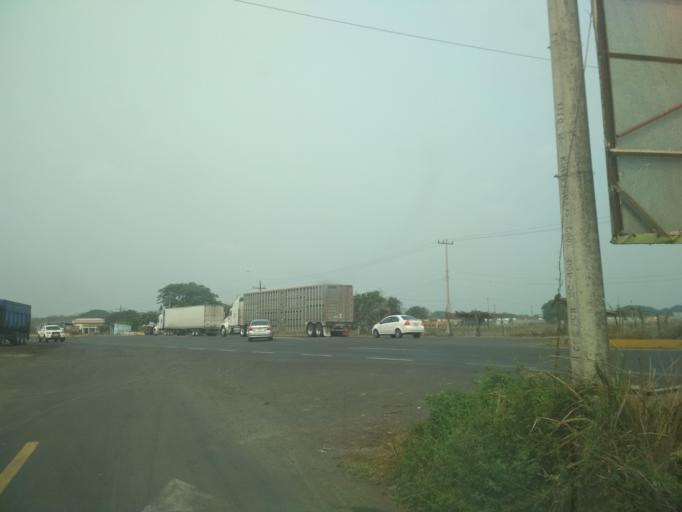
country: MX
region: Veracruz
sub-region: Veracruz
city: Delfino Victoria (Santa Fe)
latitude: 19.2226
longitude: -96.2579
